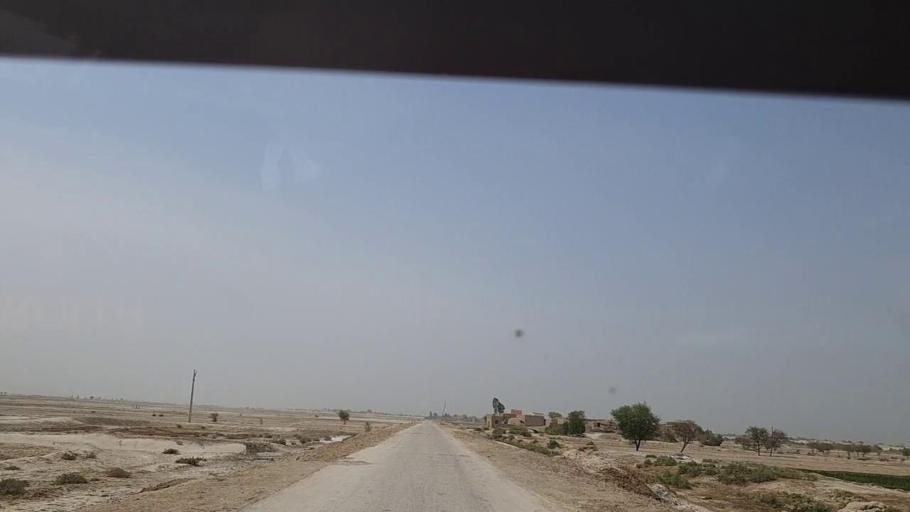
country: PK
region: Sindh
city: Khairpur Nathan Shah
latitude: 27.0614
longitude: 67.6482
